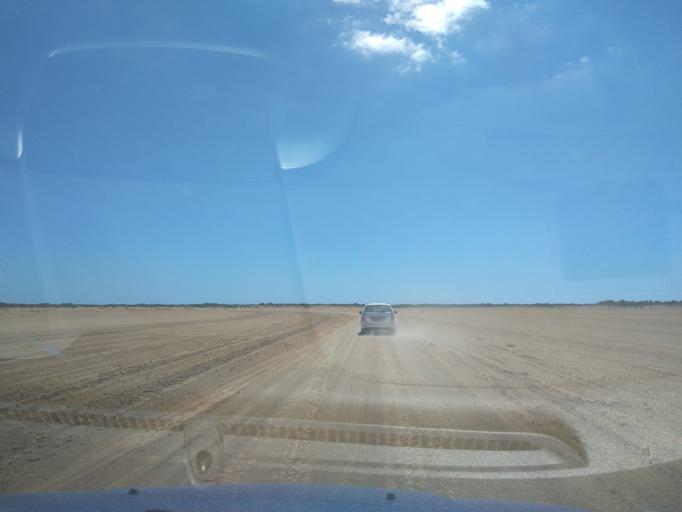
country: TN
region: Susah
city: Harqalah
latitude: 36.1626
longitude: 10.4546
